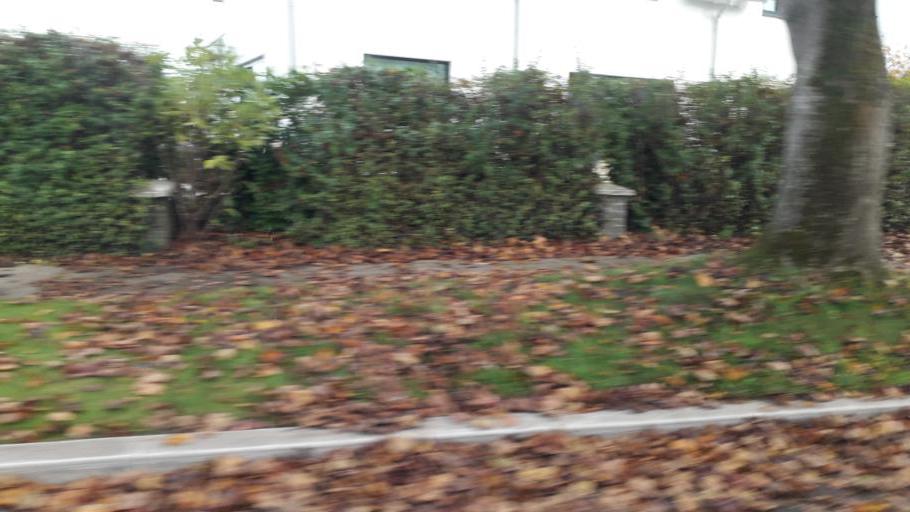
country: IE
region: Leinster
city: Mount Merrion
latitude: 53.2978
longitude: -6.2289
